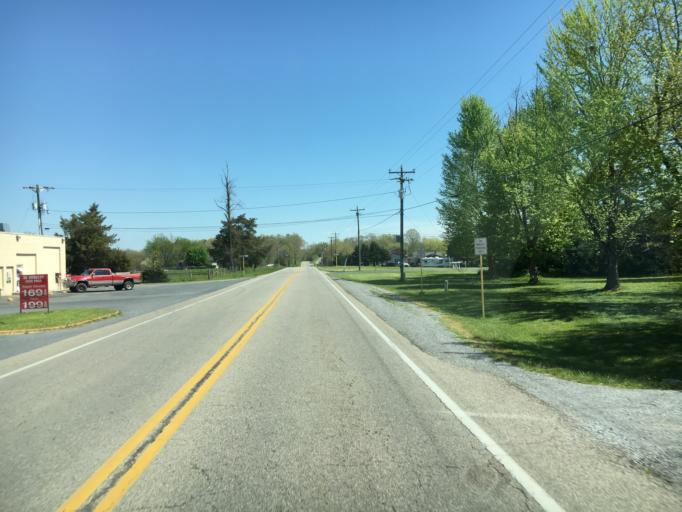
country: US
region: Virginia
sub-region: Augusta County
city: Crimora
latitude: 38.1776
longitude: -78.8457
